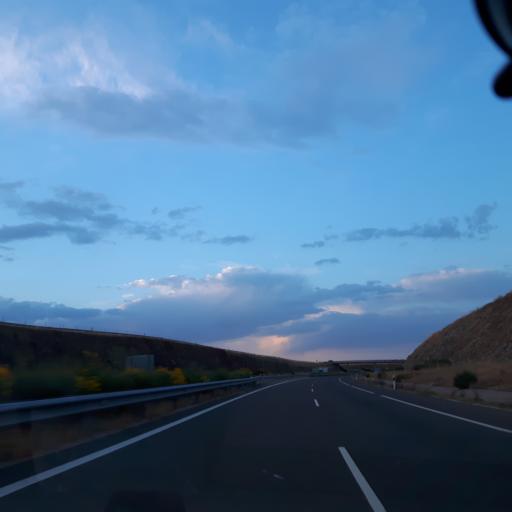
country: ES
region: Castille and Leon
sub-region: Provincia de Salamanca
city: Mozarbez
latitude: 40.8638
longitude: -5.6457
